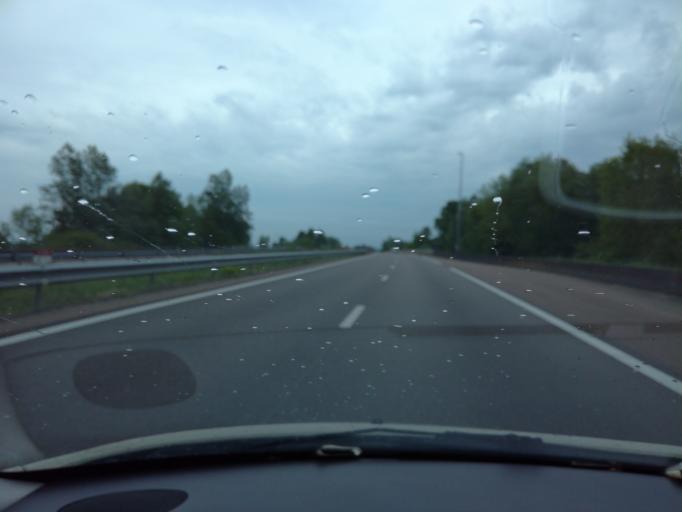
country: FR
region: Franche-Comte
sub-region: Departement du Jura
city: Choisey
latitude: 47.0427
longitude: 5.4504
